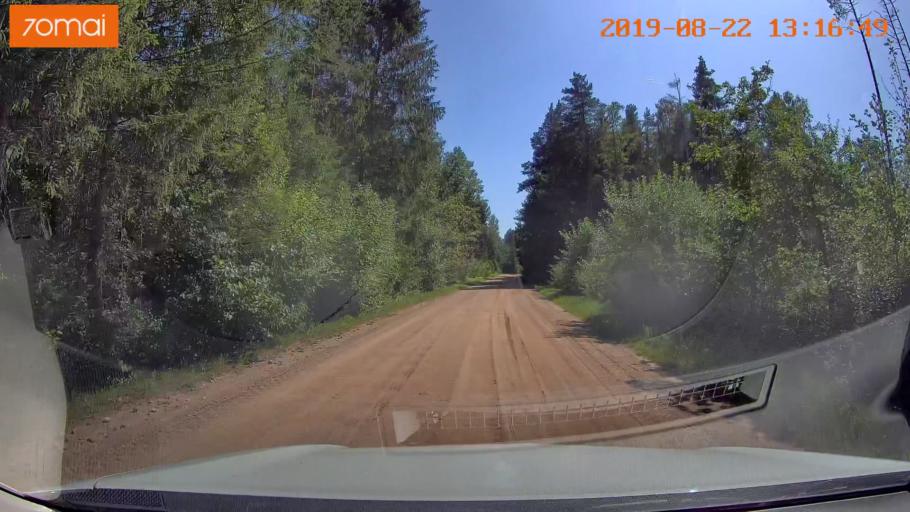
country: BY
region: Minsk
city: Prawdzinski
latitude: 53.2532
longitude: 27.9151
